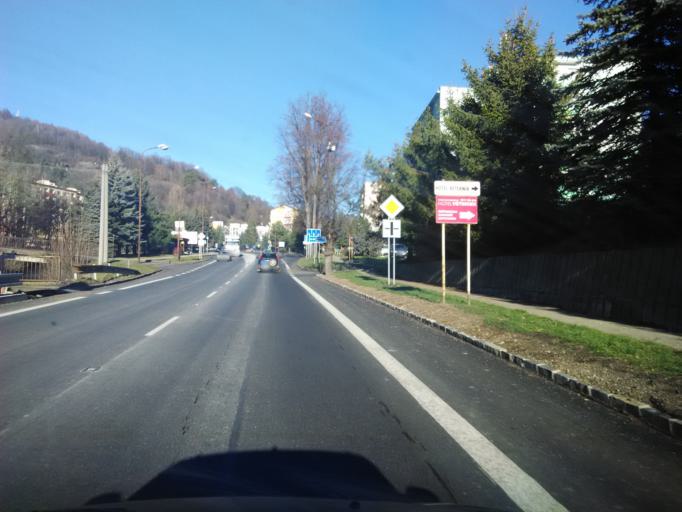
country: SK
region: Banskobystricky
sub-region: Okres Ziar nad Hronom
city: Kremnica
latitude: 48.6976
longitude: 18.9152
